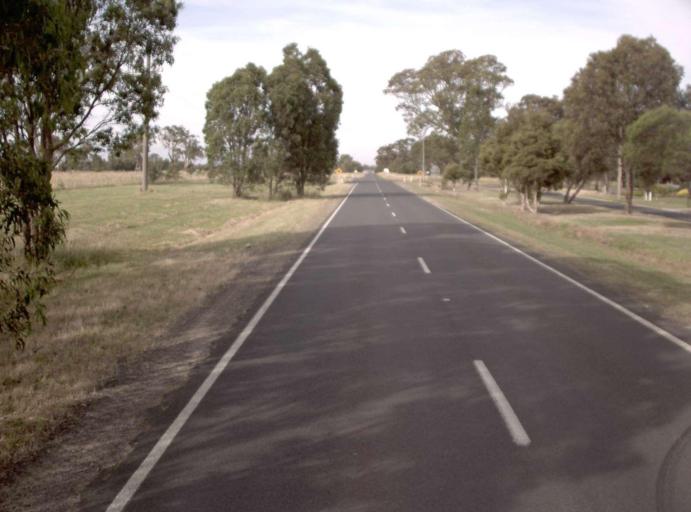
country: AU
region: Victoria
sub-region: Latrobe
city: Traralgon
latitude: -38.1205
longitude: 146.5741
